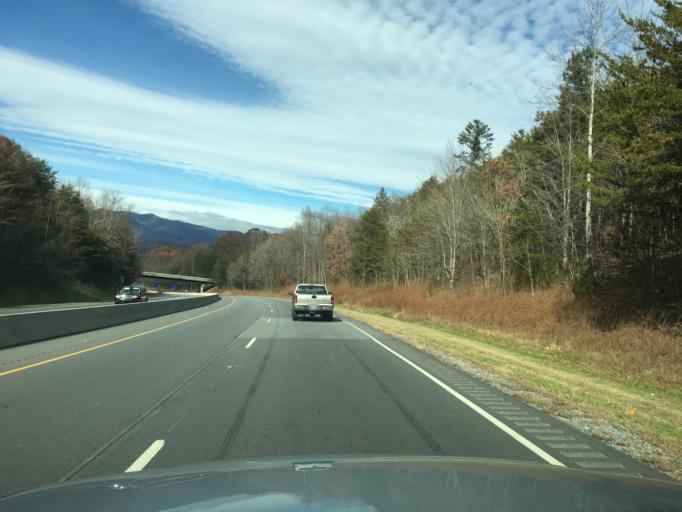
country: US
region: North Carolina
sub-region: McDowell County
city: Marion
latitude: 35.6966
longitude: -82.0300
